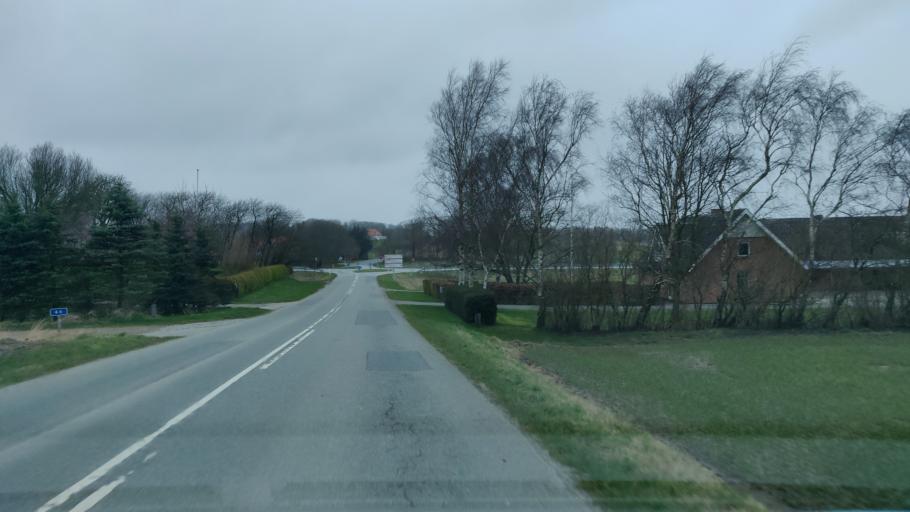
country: DK
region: Central Jutland
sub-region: Skive Kommune
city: Hojslev
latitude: 56.5900
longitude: 9.2215
